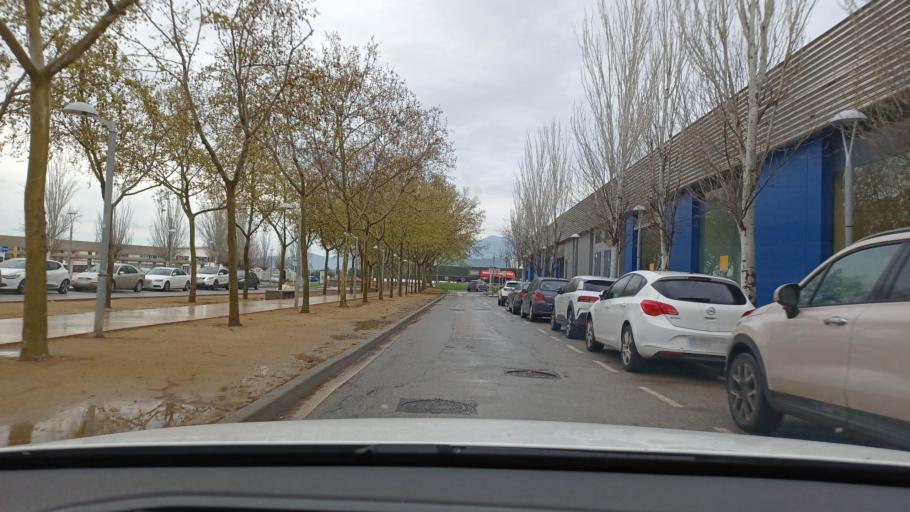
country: ES
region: Catalonia
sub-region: Provincia de Tarragona
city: Amposta
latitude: 40.7076
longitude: 0.5716
